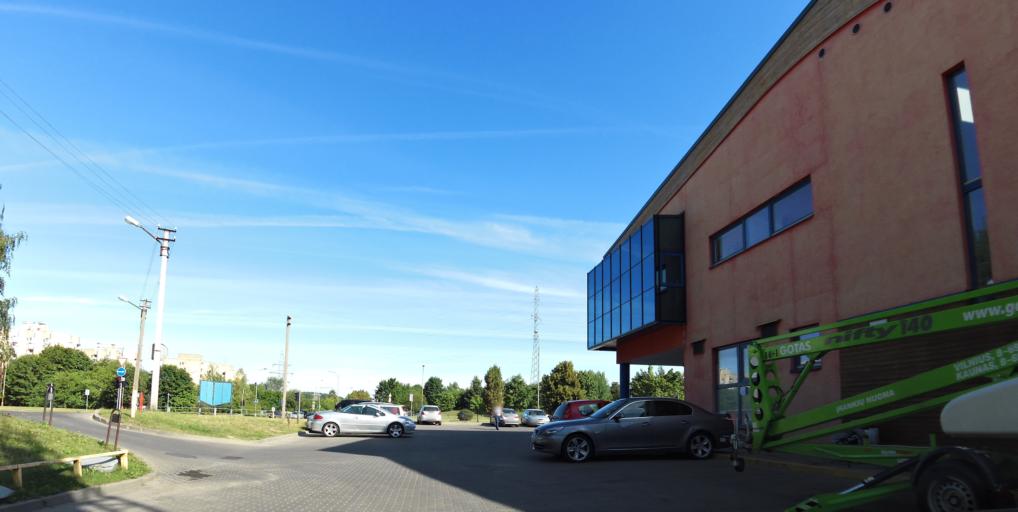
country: LT
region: Vilnius County
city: Seskine
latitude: 54.7083
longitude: 25.2410
